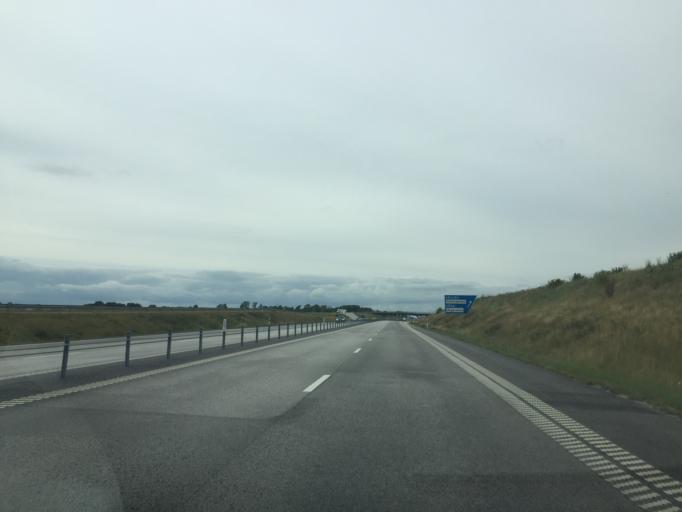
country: SE
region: Skane
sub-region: Vellinge Kommun
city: Vellinge
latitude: 55.4327
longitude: 13.0453
